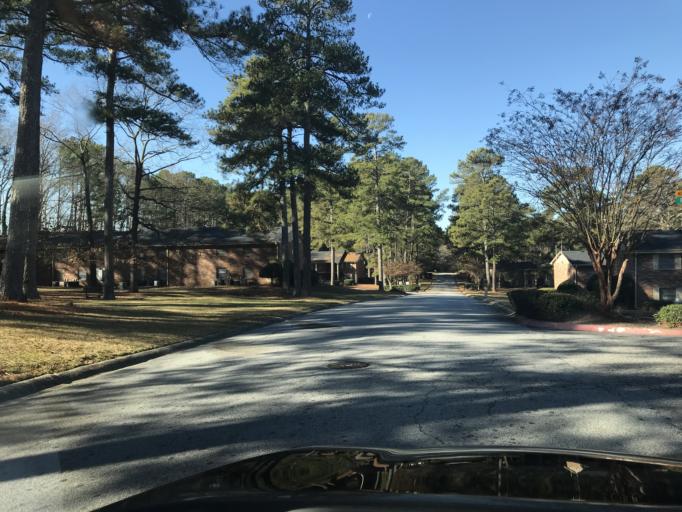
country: US
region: Georgia
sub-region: Clayton County
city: Riverdale
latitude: 33.5628
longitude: -84.3756
